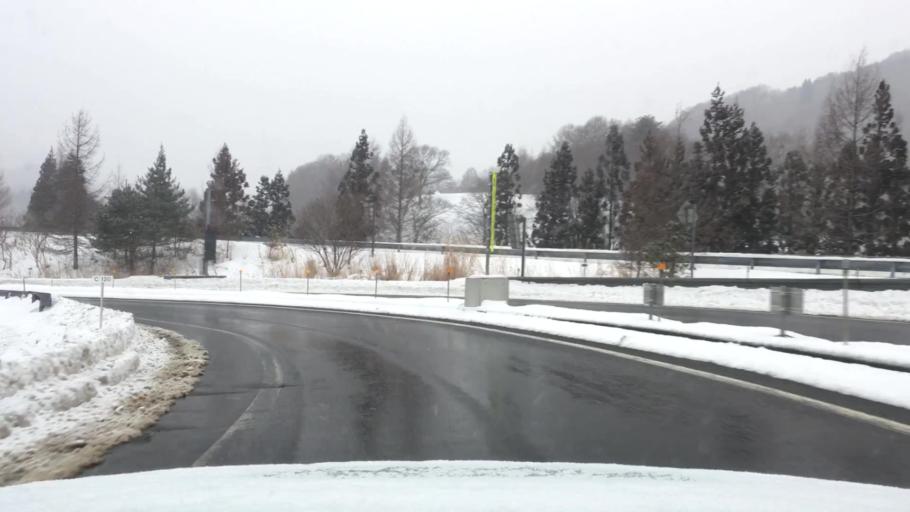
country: JP
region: Iwate
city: Ichinohe
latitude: 40.1105
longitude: 141.0491
